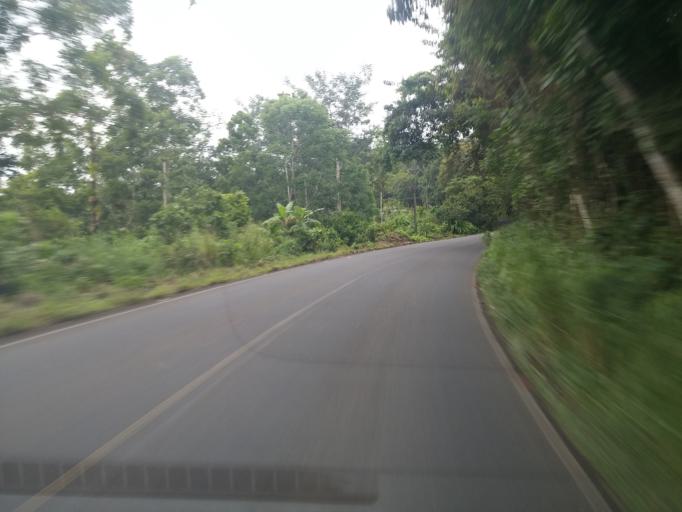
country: CR
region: Alajuela
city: Bijagua
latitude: 10.8099
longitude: -85.0161
